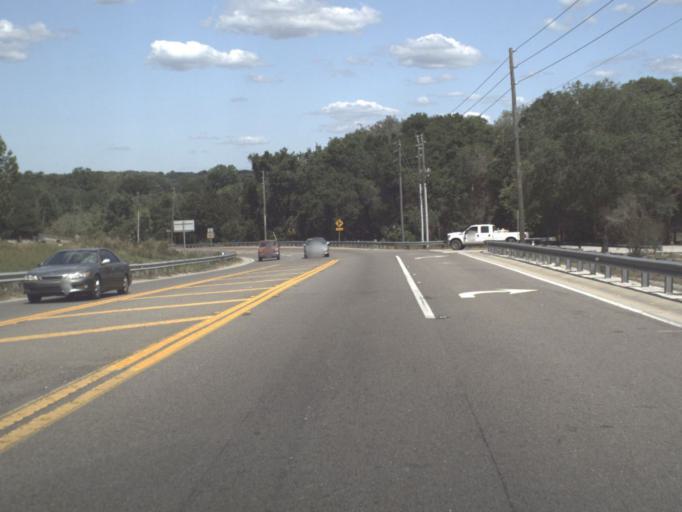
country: US
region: Florida
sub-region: Lake County
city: Mount Dora
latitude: 28.7969
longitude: -81.6237
